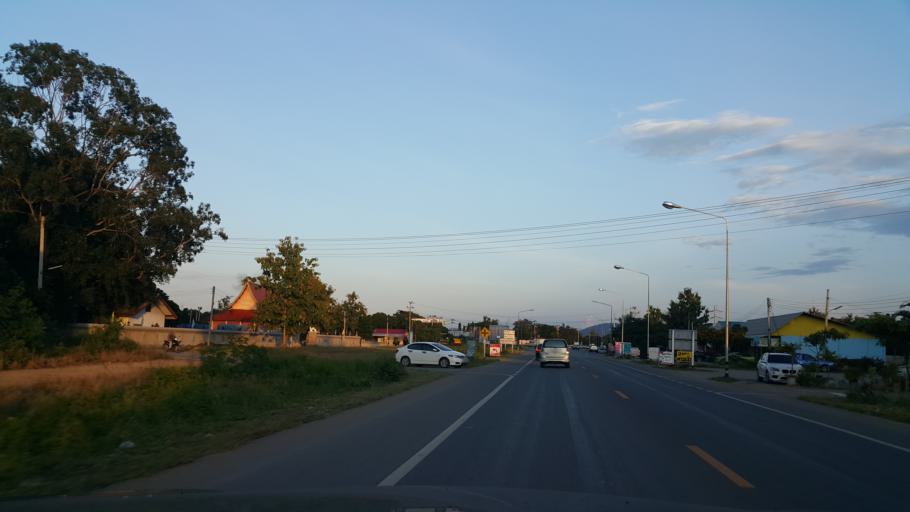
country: TH
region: Lamphun
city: Pa Sang
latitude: 18.4868
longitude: 98.9353
